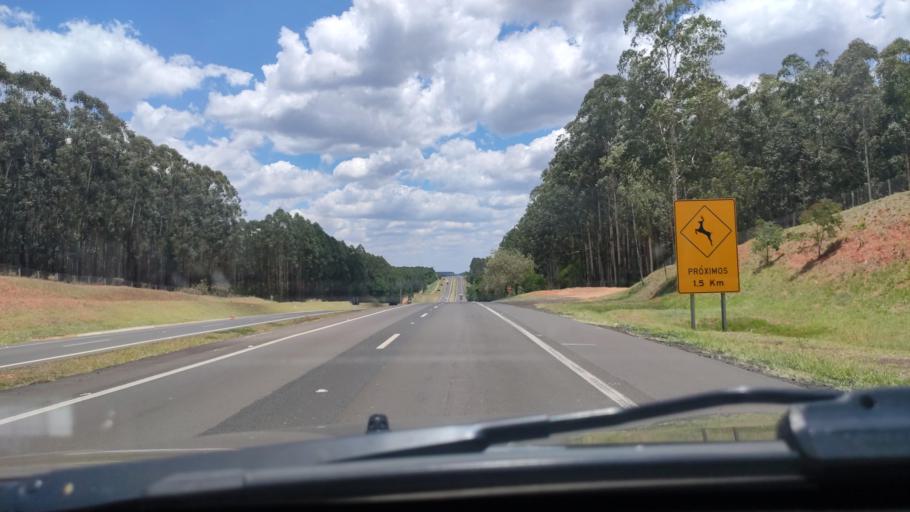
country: BR
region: Sao Paulo
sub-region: Duartina
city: Duartina
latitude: -22.4905
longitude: -49.2499
